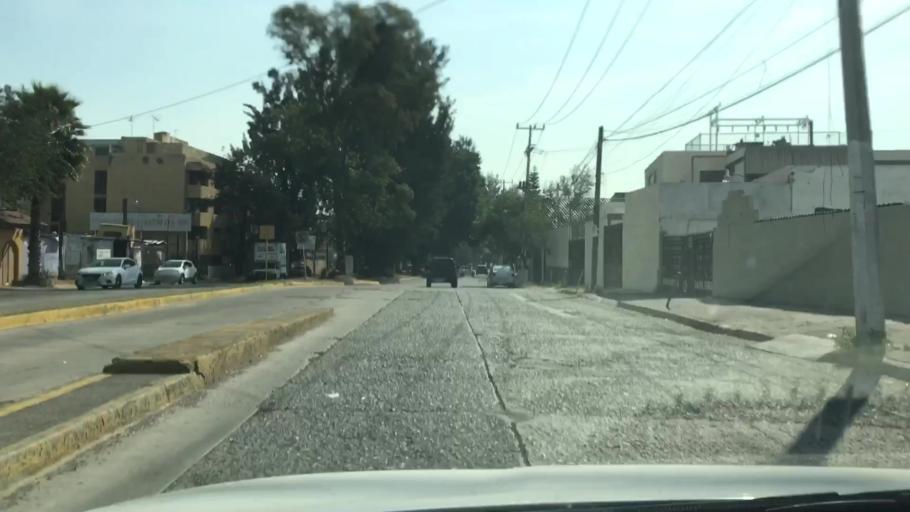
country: MX
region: Jalisco
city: Guadalajara
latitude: 20.6459
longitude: -103.4041
